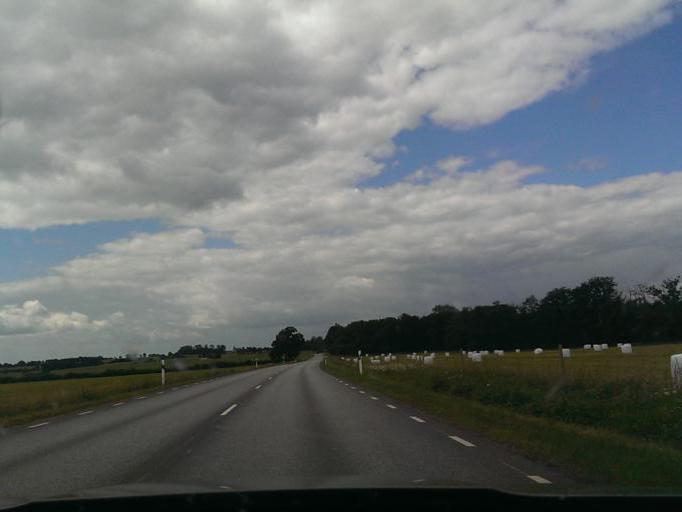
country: SE
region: Skane
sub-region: Eslovs Kommun
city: Stehag
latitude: 55.9096
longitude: 13.3525
